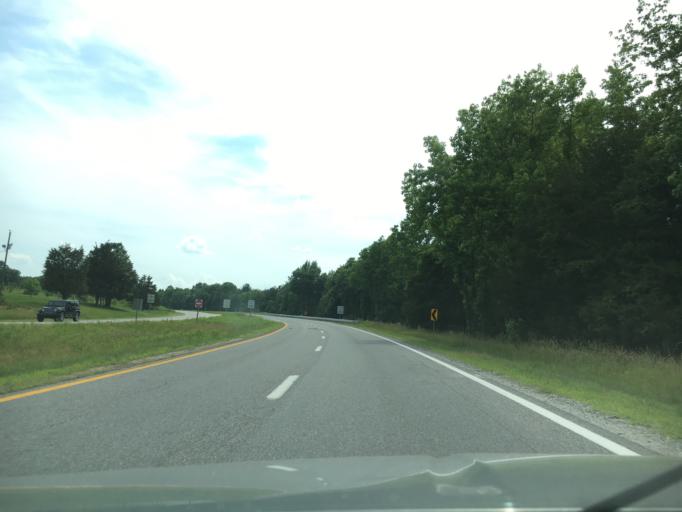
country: US
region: Virginia
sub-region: Prince Edward County
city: Hampden Sydney
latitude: 37.1054
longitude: -78.3688
